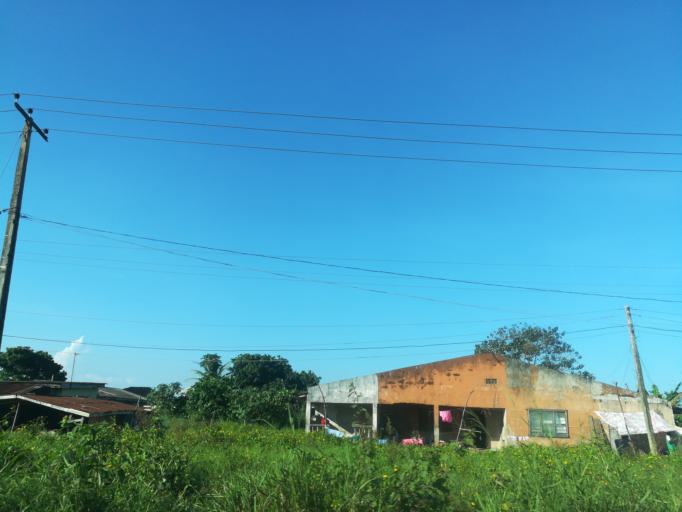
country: NG
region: Lagos
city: Ebute Ikorodu
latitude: 6.5411
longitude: 3.5479
